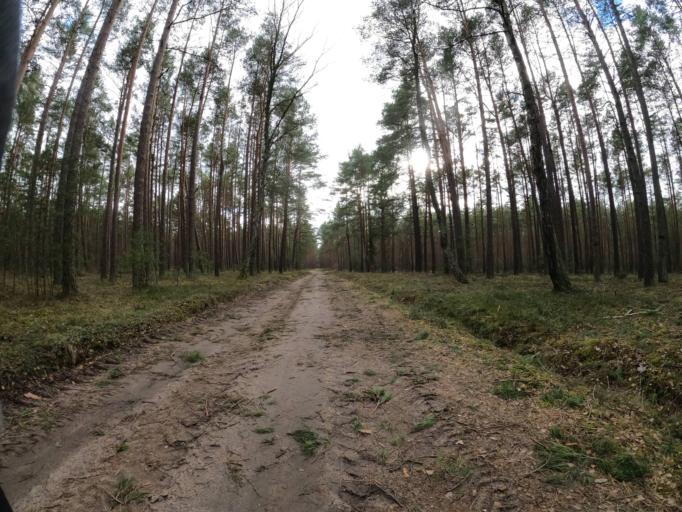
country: PL
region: Greater Poland Voivodeship
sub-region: Powiat zlotowski
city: Sypniewo
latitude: 53.4405
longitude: 16.5294
